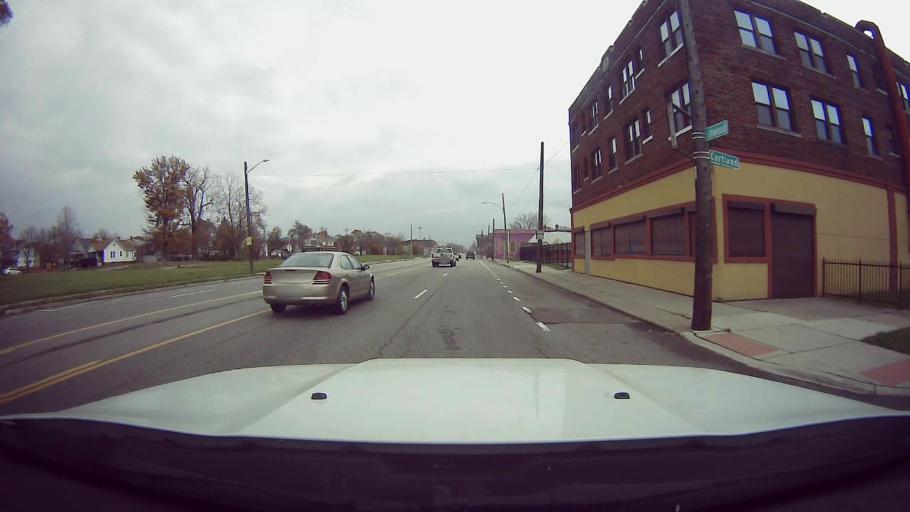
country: US
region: Michigan
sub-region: Wayne County
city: Highland Park
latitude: 42.3869
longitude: -83.1180
